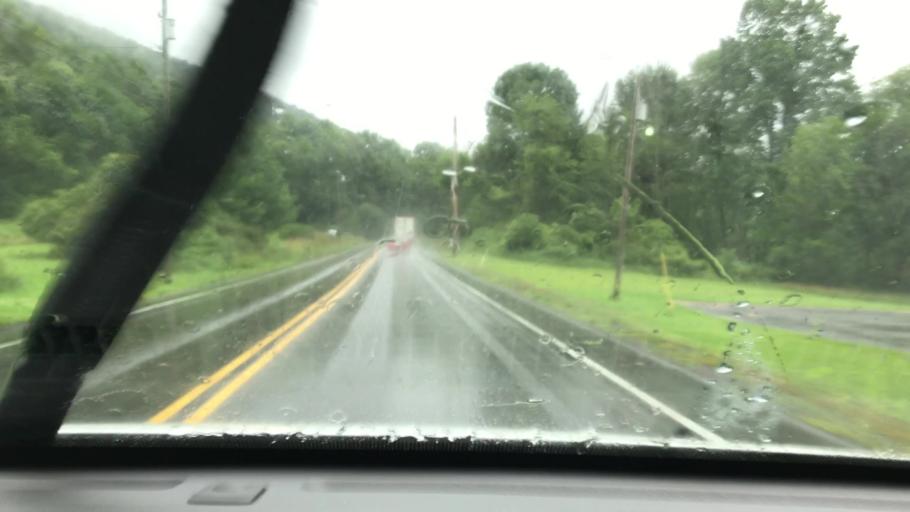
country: US
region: Pennsylvania
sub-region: Blair County
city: Tyrone
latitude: 40.7510
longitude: -78.2170
